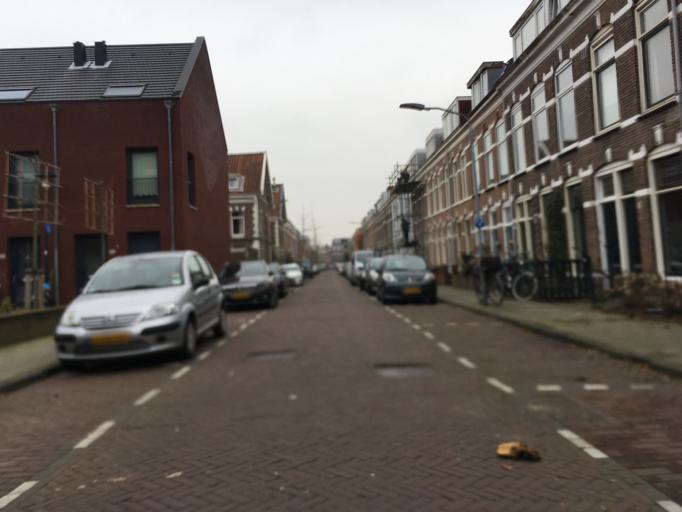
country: NL
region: North Holland
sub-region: Gemeente Haarlem
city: Haarlem
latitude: 52.3927
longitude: 4.6359
